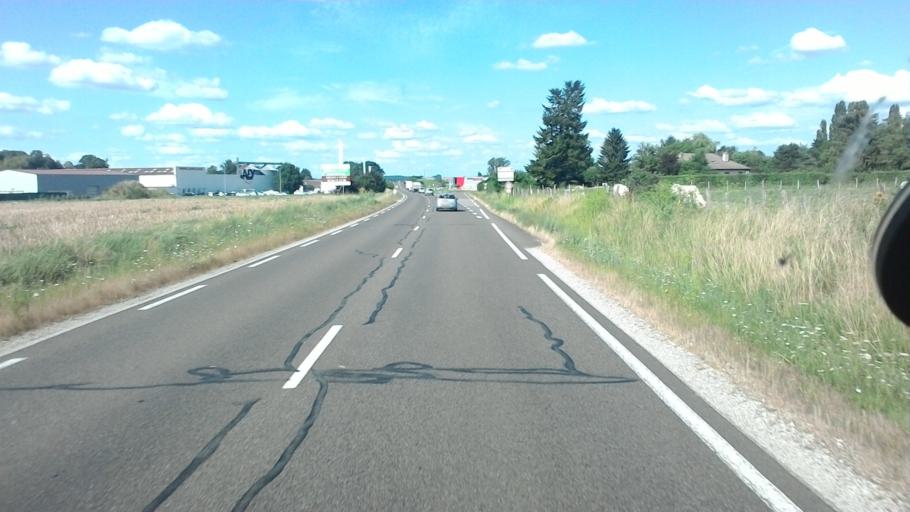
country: FR
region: Franche-Comte
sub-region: Departement de la Haute-Saone
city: Gy
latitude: 47.4107
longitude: 5.8091
